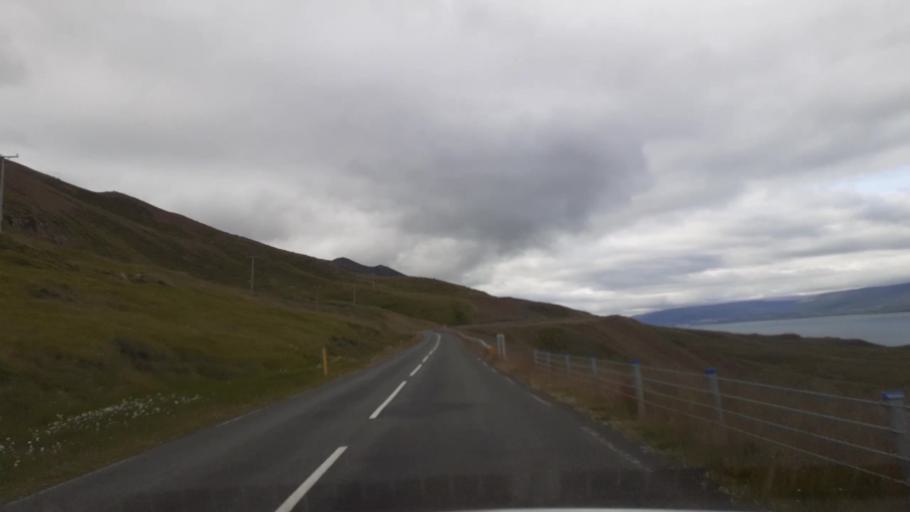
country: IS
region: Northeast
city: Akureyri
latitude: 65.8388
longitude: -18.0559
